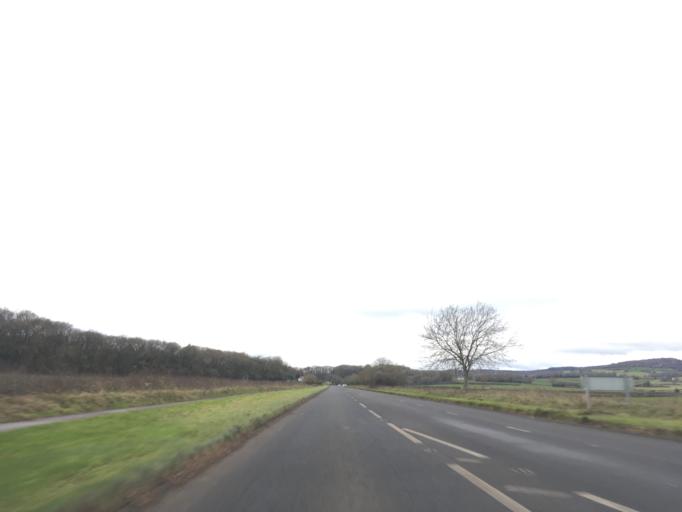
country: GB
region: Wales
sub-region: Monmouthshire
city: Rogiet
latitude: 51.6128
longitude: -2.7864
